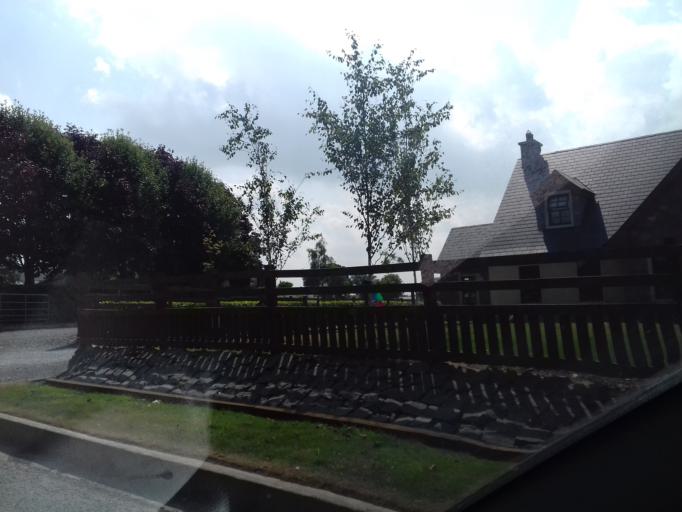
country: IE
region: Leinster
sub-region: An Mhi
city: Stamullin
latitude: 53.5912
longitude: -6.2927
